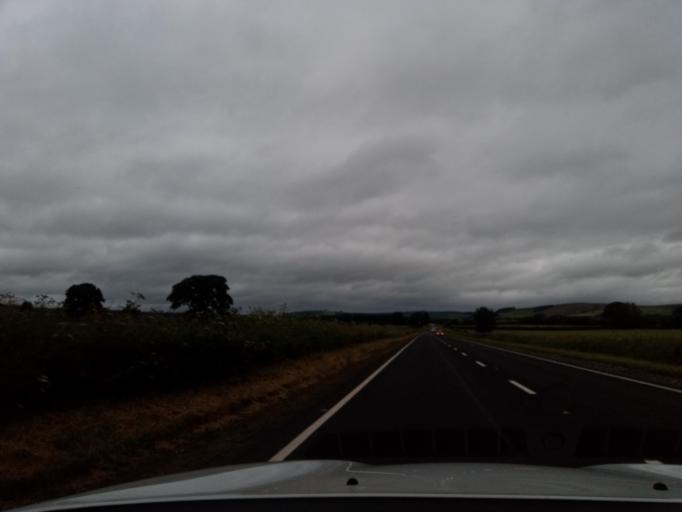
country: GB
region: Scotland
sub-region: The Scottish Borders
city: Lauder
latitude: 55.7416
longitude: -2.7687
